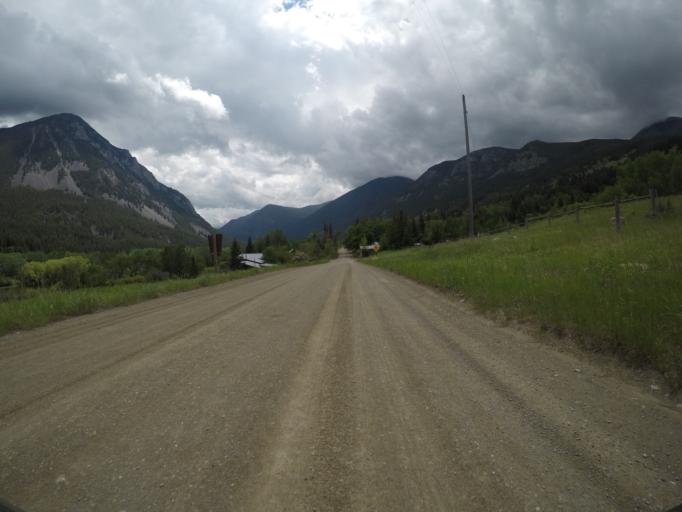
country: US
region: Montana
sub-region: Park County
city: Livingston
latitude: 45.5235
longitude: -110.2241
